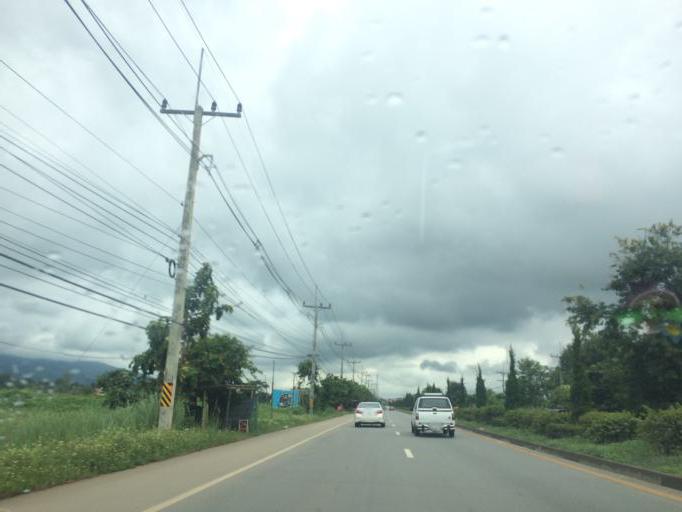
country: TH
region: Chiang Rai
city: Mae Chan
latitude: 20.0344
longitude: 99.8745
